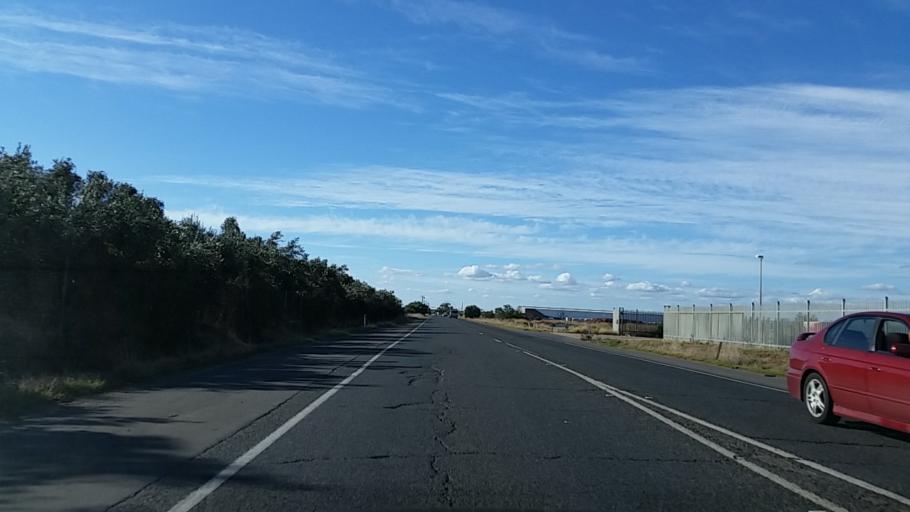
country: AU
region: South Australia
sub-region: Salisbury
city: Salisbury
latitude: -34.7293
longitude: 138.5917
